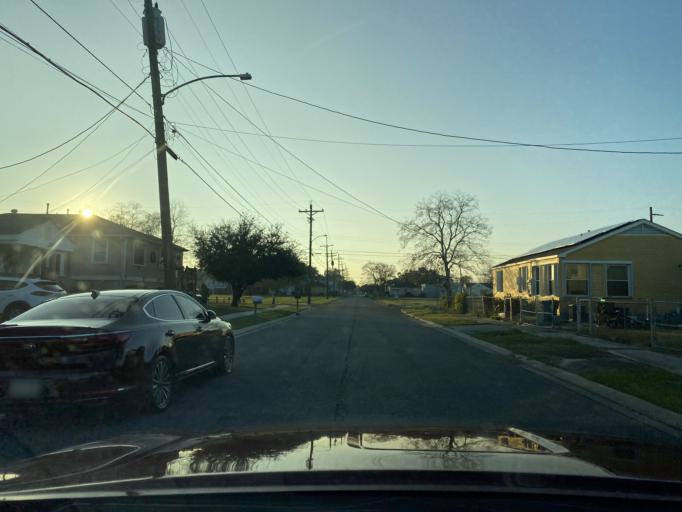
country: US
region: Louisiana
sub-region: Orleans Parish
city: New Orleans
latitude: 30.0214
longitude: -90.0534
